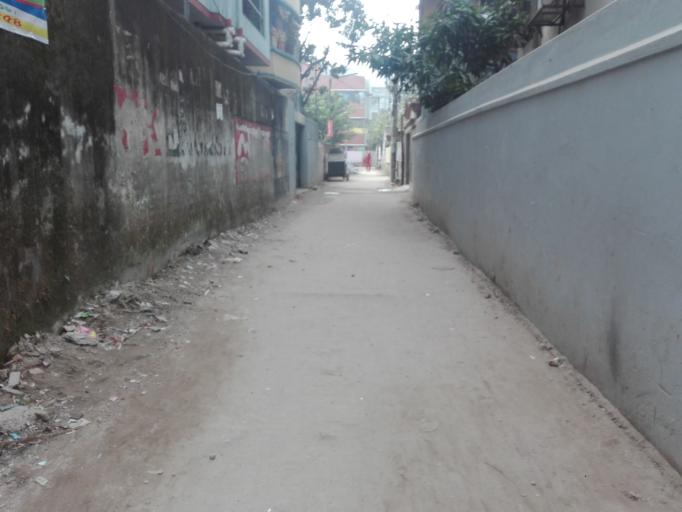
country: BD
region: Dhaka
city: Azimpur
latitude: 23.7933
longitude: 90.3589
